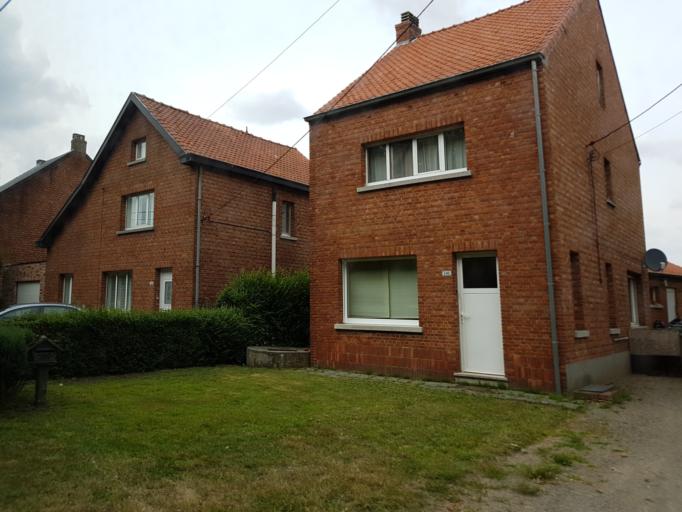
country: BE
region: Flanders
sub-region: Provincie Antwerpen
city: Westerlo
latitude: 51.1046
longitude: 4.8797
